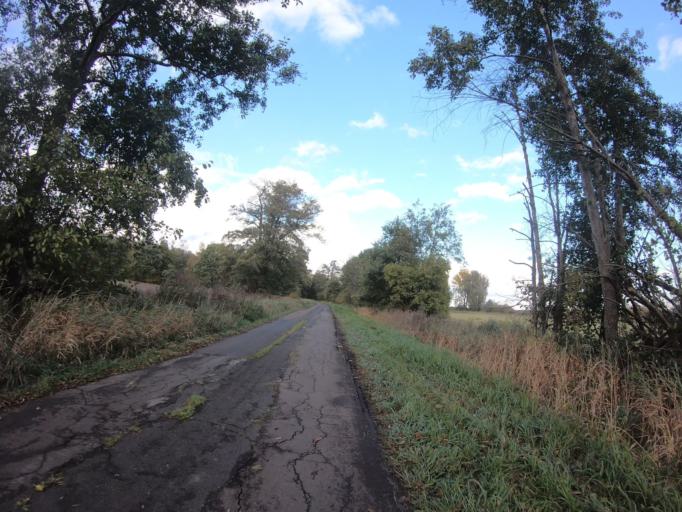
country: DE
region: Lower Saxony
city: Wagenhoff
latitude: 52.5412
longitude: 10.5551
